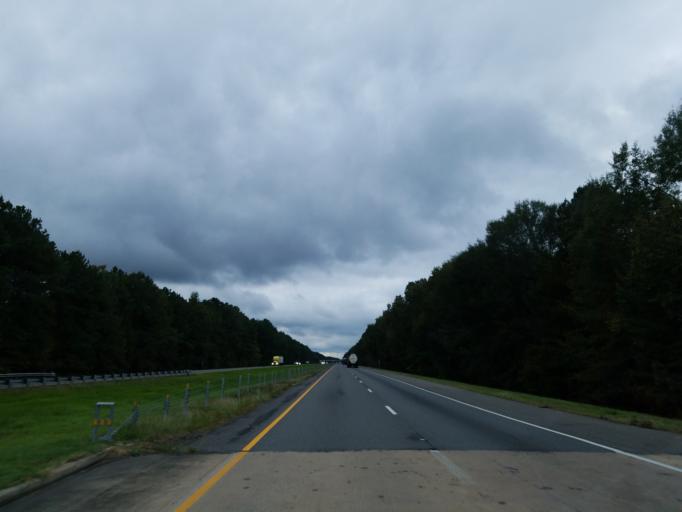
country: US
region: Alabama
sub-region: Greene County
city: Eutaw
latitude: 32.7686
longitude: -88.0631
